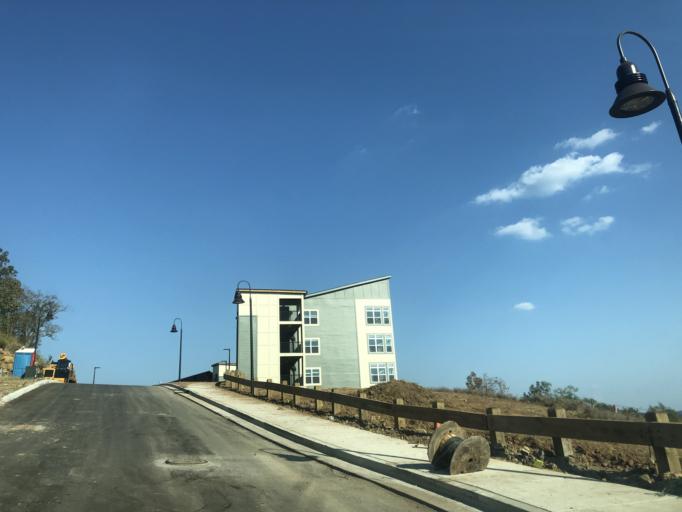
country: US
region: Tennessee
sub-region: Davidson County
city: Belle Meade
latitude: 36.1331
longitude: -86.9000
